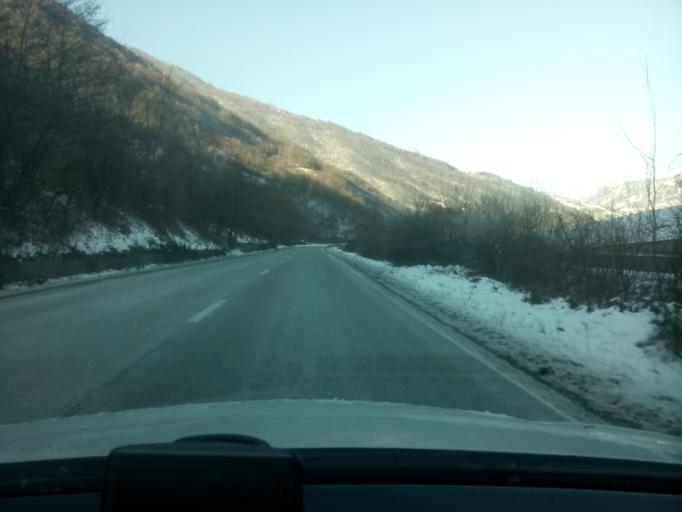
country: RO
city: Cainenii Mici
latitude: 45.4563
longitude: 24.2893
